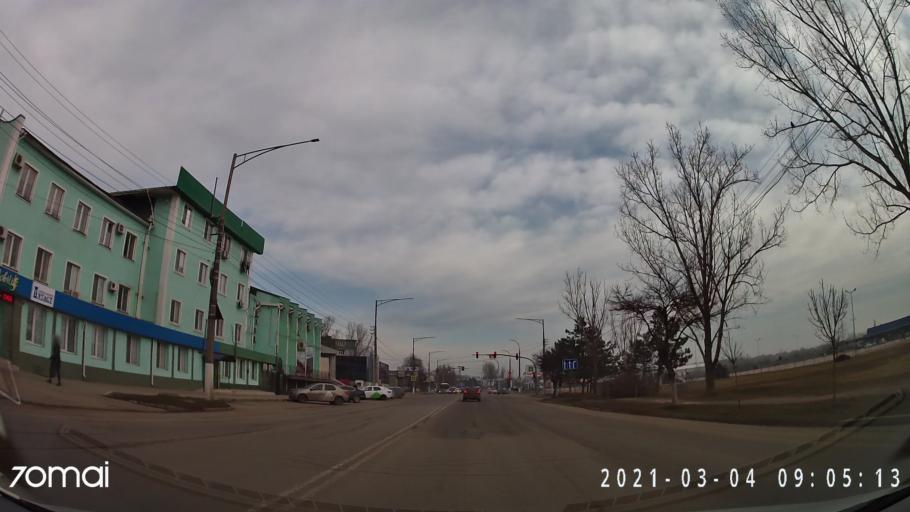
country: MD
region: Balti
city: Balti
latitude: 47.7648
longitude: 27.9414
